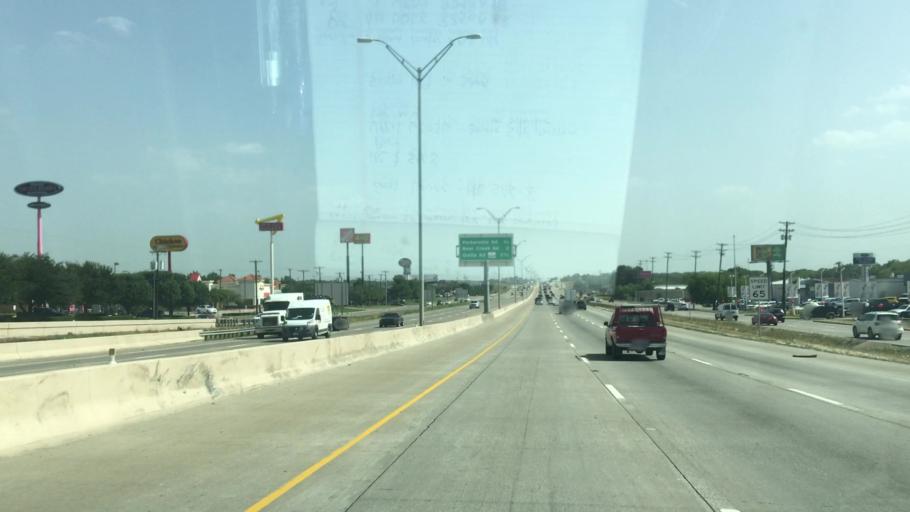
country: US
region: Texas
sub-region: Dallas County
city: DeSoto
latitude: 32.5988
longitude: -96.8226
